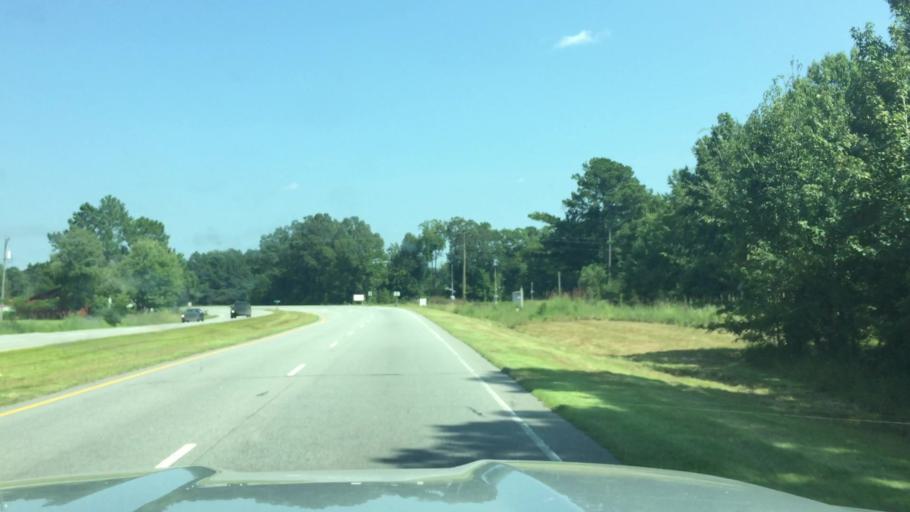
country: US
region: North Carolina
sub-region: Martin County
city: Williamston
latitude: 35.8072
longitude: -76.9429
